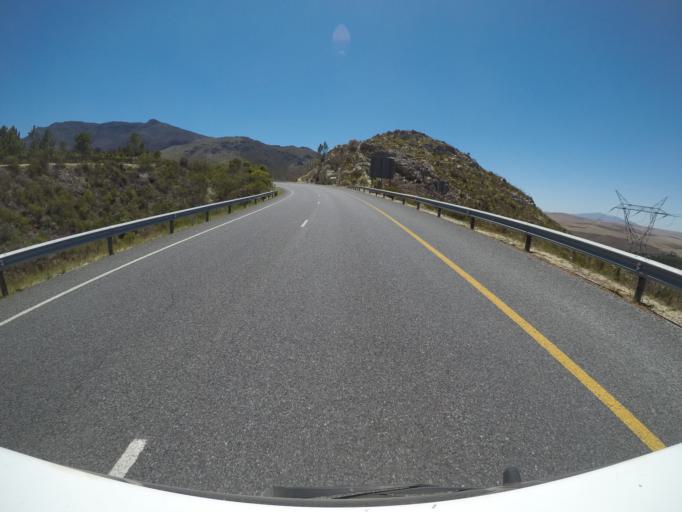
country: ZA
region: Western Cape
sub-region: Overberg District Municipality
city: Grabouw
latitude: -34.2203
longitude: 19.1890
